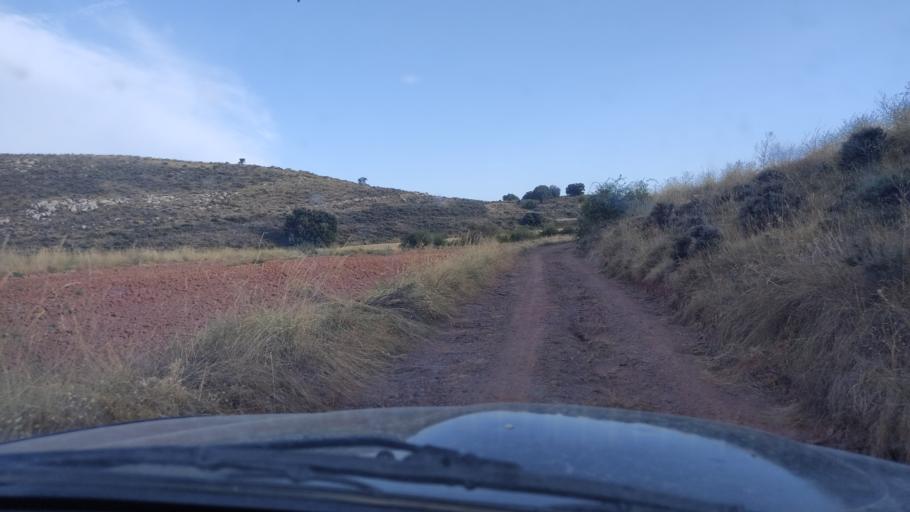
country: ES
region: Aragon
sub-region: Provincia de Teruel
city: Monforte de Moyuela
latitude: 41.0273
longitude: -1.0076
